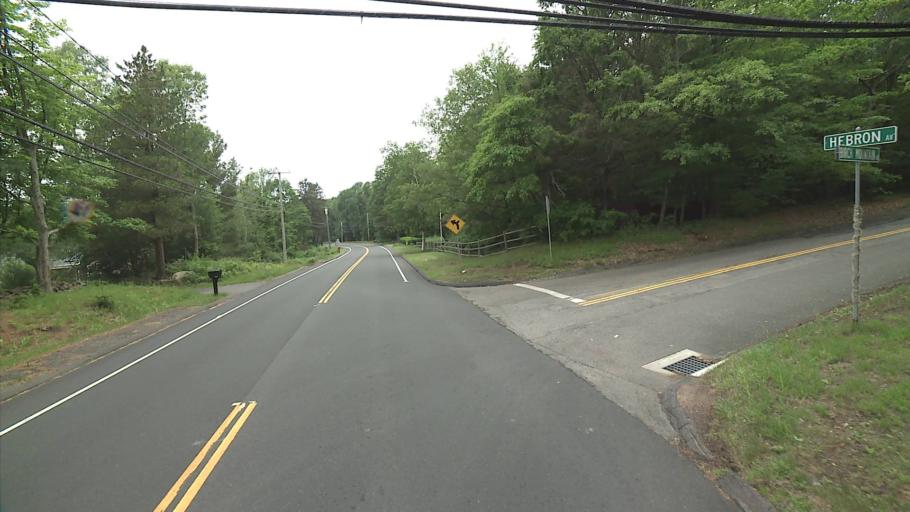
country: US
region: Connecticut
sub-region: Hartford County
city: Terramuggus
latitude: 41.7068
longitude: -72.4744
